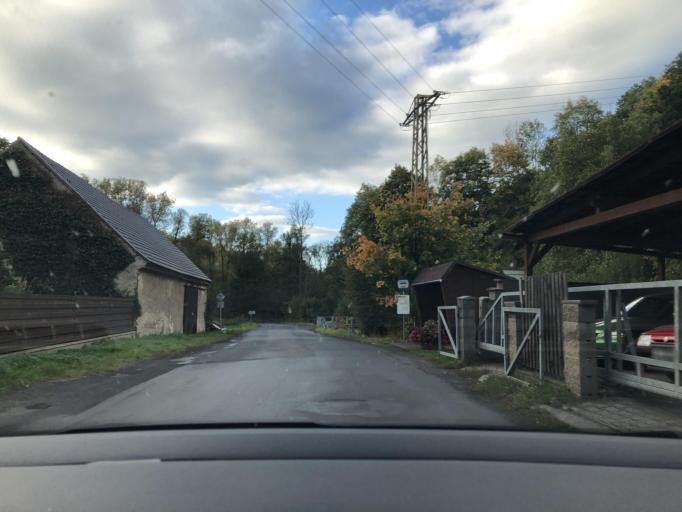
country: CZ
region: Ustecky
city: Velke Brezno
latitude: 50.6419
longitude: 14.1510
